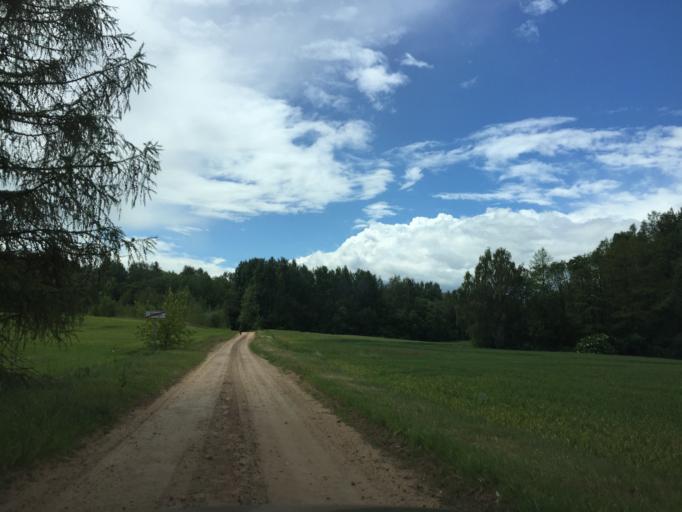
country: LV
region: Lecava
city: Iecava
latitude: 56.5563
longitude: 24.1580
